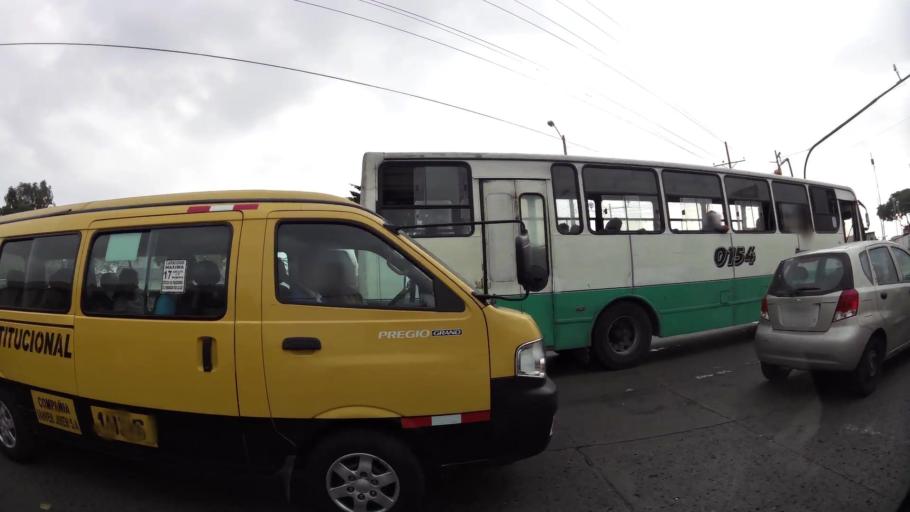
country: EC
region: Guayas
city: Eloy Alfaro
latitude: -2.1325
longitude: -79.8887
